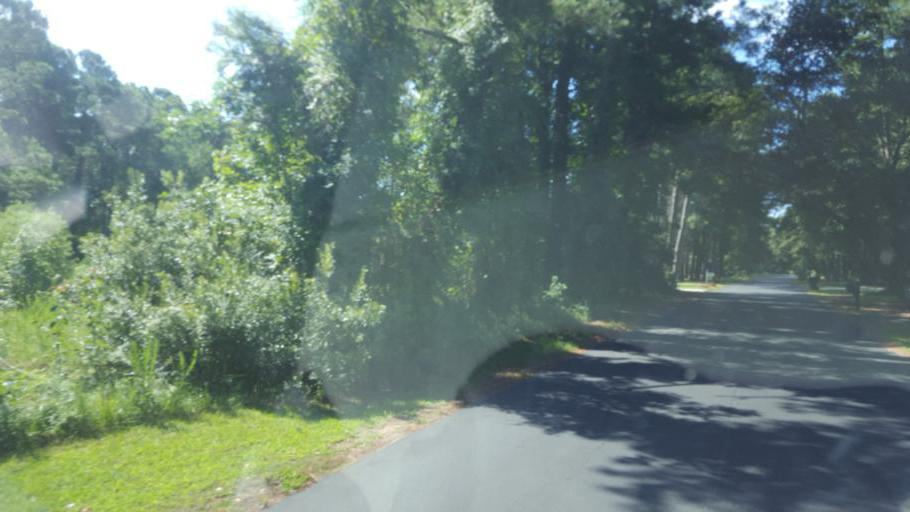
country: US
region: North Carolina
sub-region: Dare County
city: Kill Devil Hills
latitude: 36.0121
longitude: -75.6768
